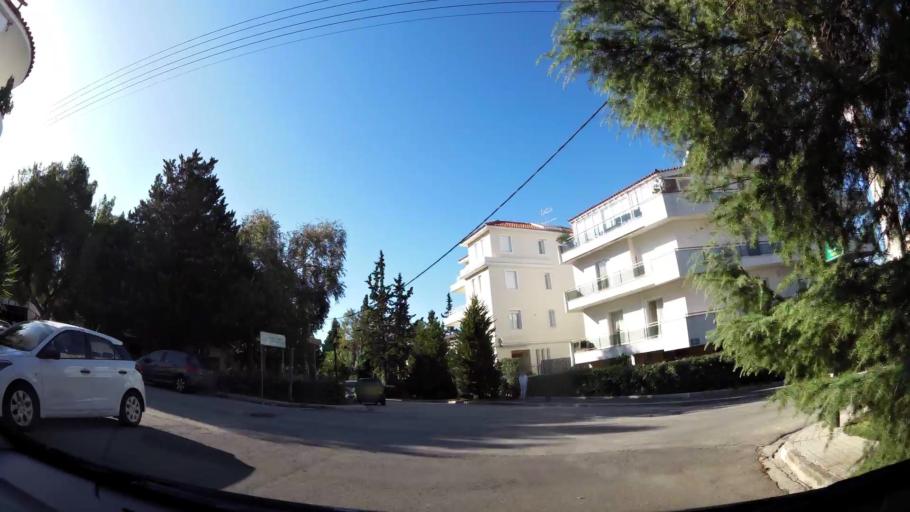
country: GR
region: Attica
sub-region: Nomarchia Anatolikis Attikis
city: Voula
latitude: 37.8546
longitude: 23.7708
